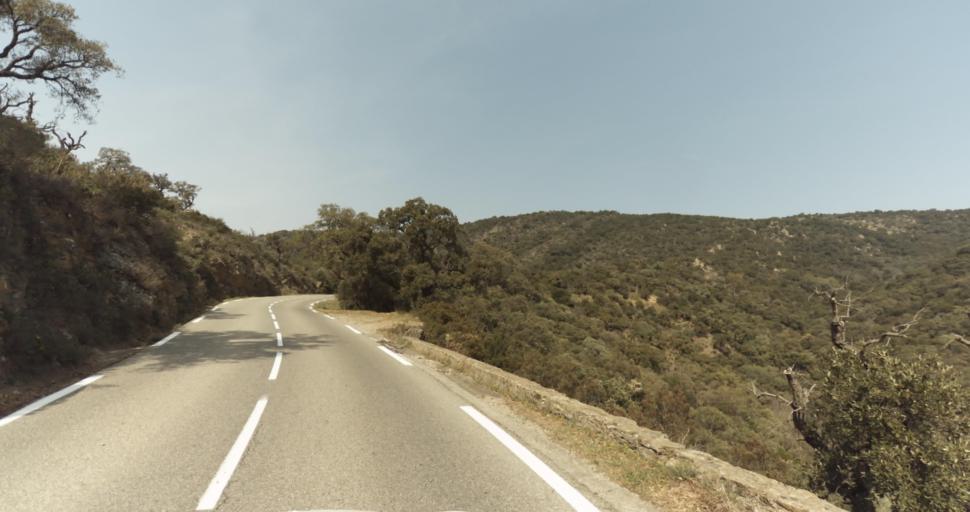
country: FR
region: Provence-Alpes-Cote d'Azur
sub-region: Departement du Var
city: Bormes-les-Mimosas
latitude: 43.1596
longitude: 6.3438
